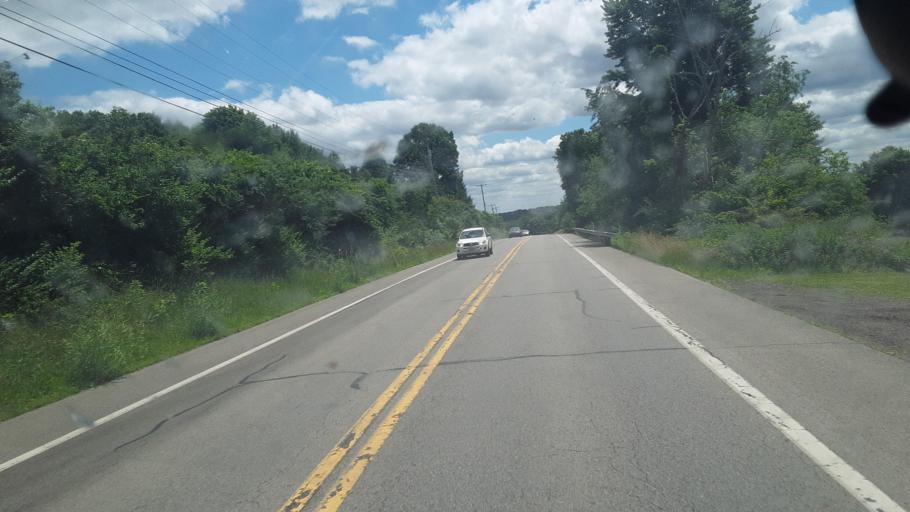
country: US
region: Pennsylvania
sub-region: Butler County
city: Slippery Rock
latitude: 40.9923
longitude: -80.1708
